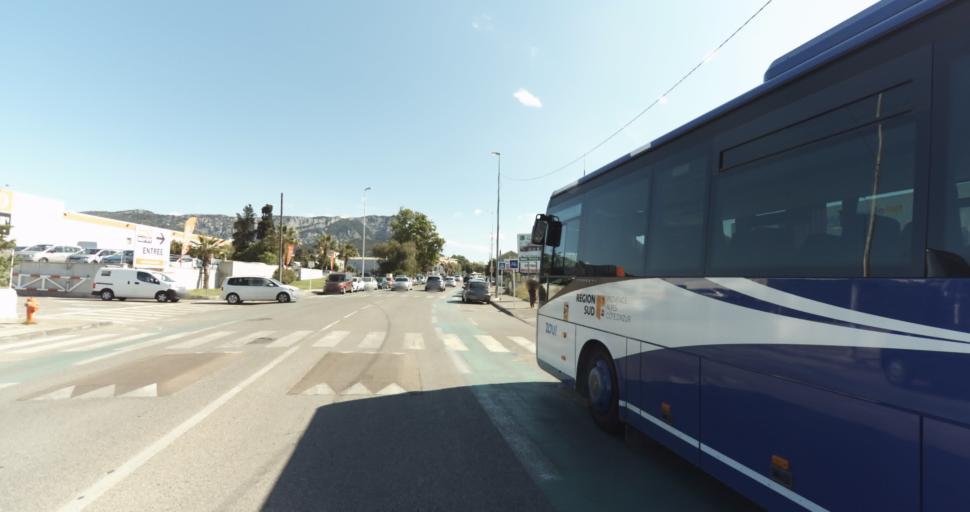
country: FR
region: Provence-Alpes-Cote d'Azur
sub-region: Departement du Var
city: La Valette-du-Var
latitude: 43.1263
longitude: 5.9762
